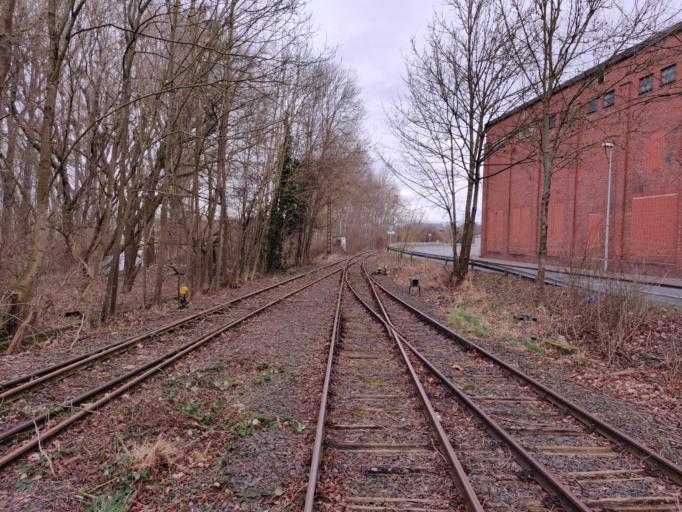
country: DE
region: Lower Saxony
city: Bockenem
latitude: 52.0137
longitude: 10.1230
